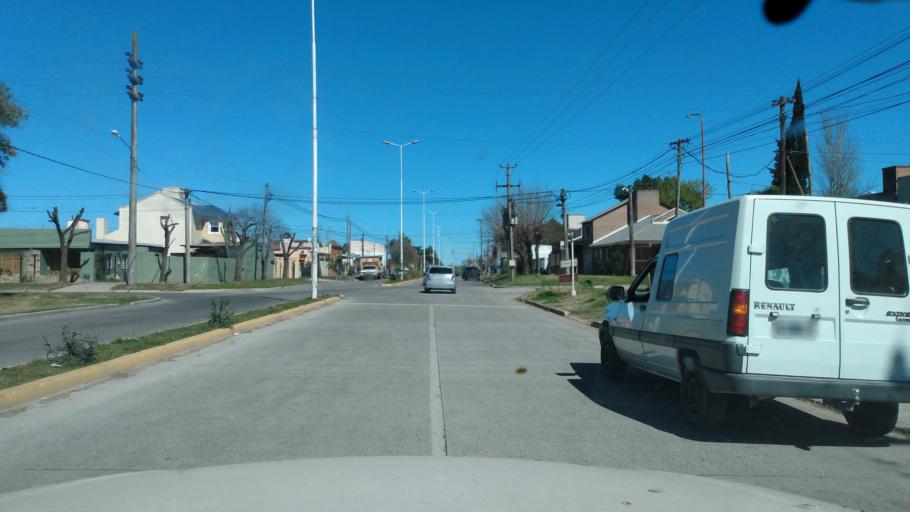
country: AR
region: Buenos Aires
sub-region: Partido de Lujan
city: Lujan
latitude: -34.5574
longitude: -59.1024
